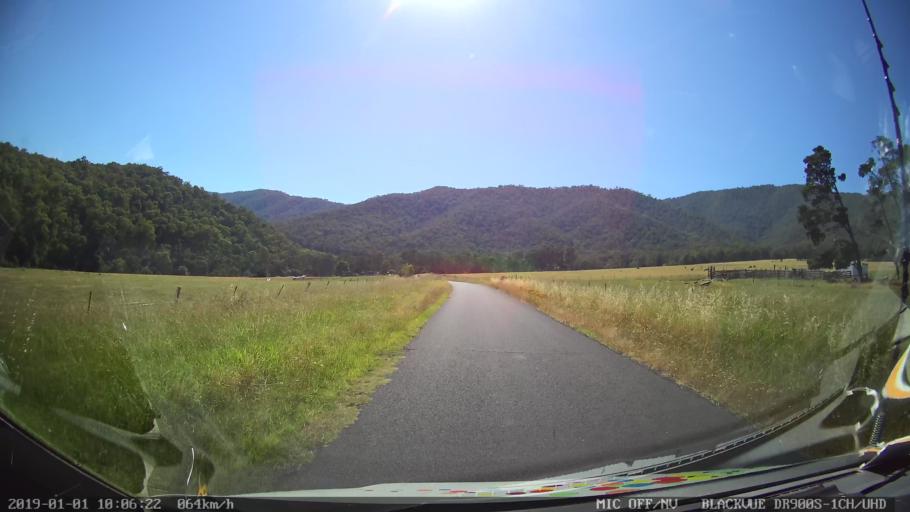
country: AU
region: New South Wales
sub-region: Snowy River
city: Jindabyne
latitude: -36.1744
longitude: 148.1468
